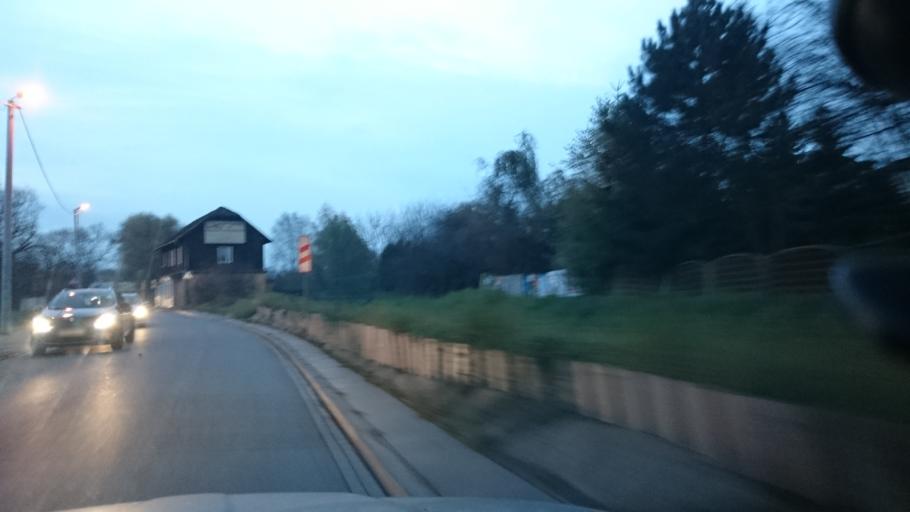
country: PL
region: Lesser Poland Voivodeship
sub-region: Powiat wielicki
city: Czarnochowice
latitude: 50.0191
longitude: 20.0363
